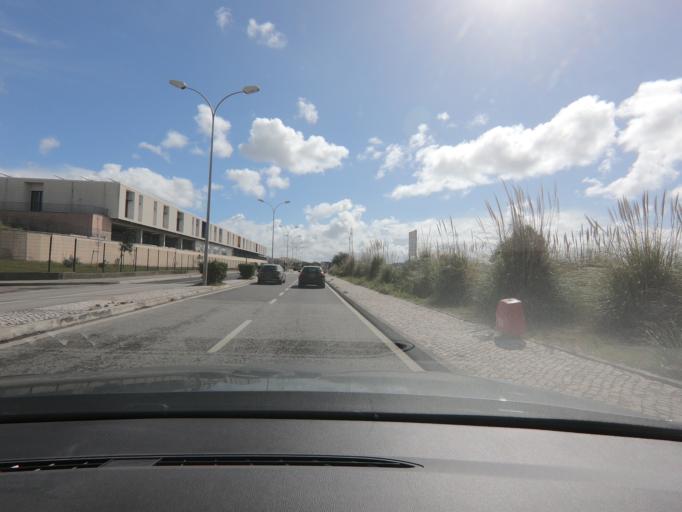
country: PT
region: Lisbon
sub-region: Oeiras
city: Porto Salvo
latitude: 38.7140
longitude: -9.3067
